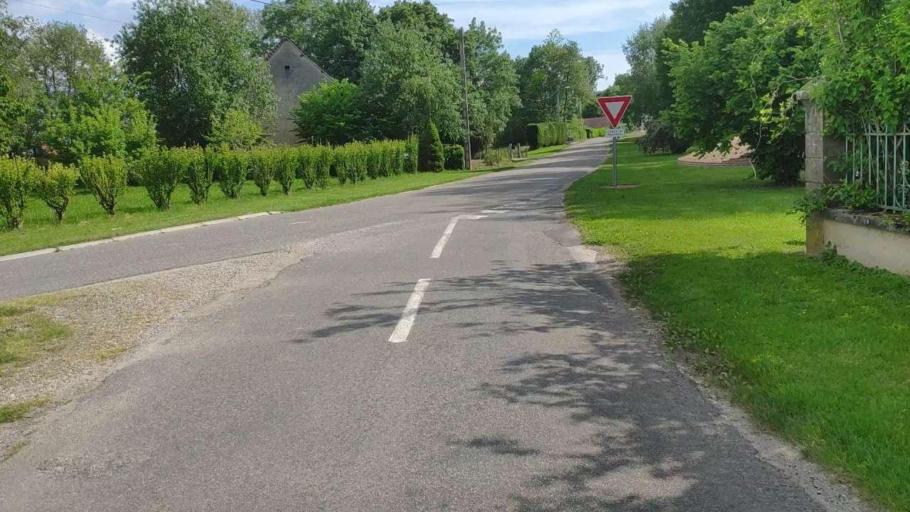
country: FR
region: Franche-Comte
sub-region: Departement du Jura
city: Bletterans
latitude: 46.8049
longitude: 5.3798
